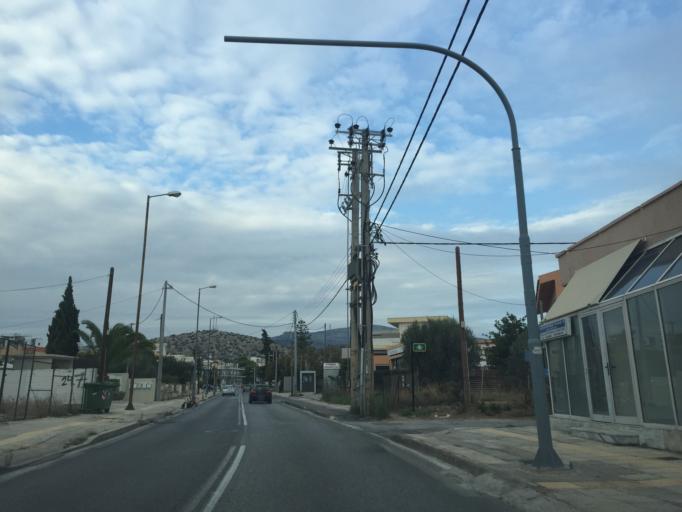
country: GR
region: Attica
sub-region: Nomarchia Anatolikis Attikis
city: Vari
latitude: 37.8274
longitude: 23.8038
